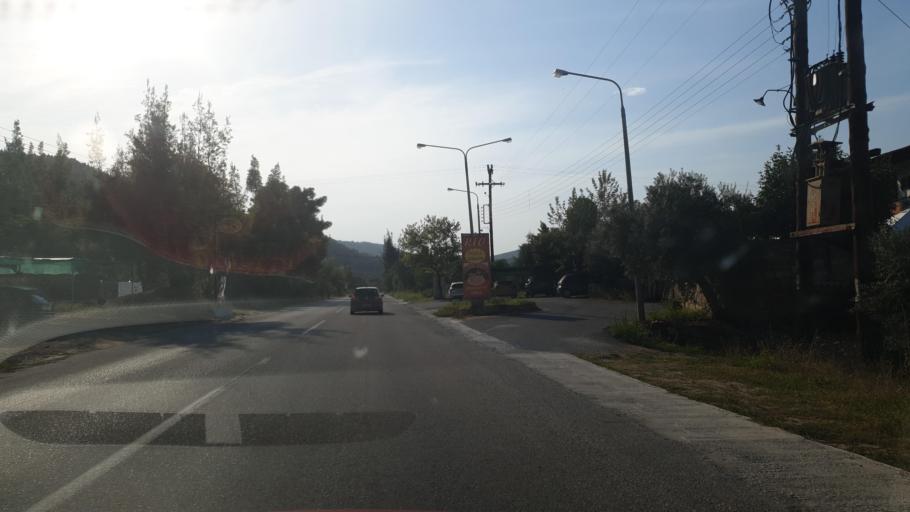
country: GR
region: Central Macedonia
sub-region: Nomos Chalkidikis
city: Neos Marmaras
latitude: 40.1839
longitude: 23.7861
